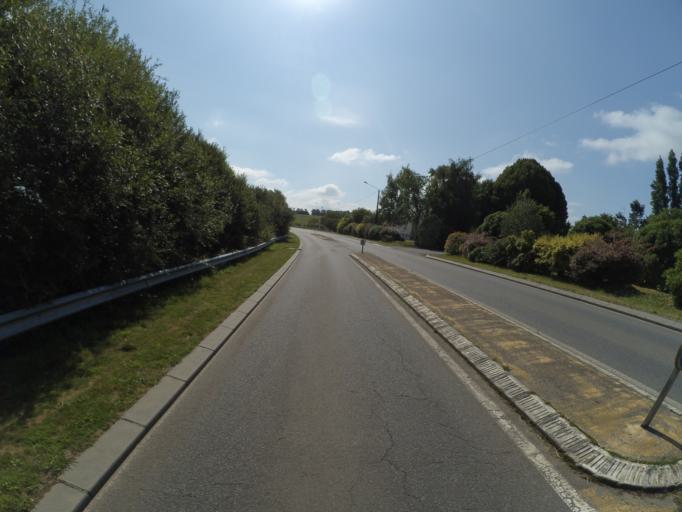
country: FR
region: Brittany
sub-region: Departement du Finistere
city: Bannalec
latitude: 47.9261
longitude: -3.6858
